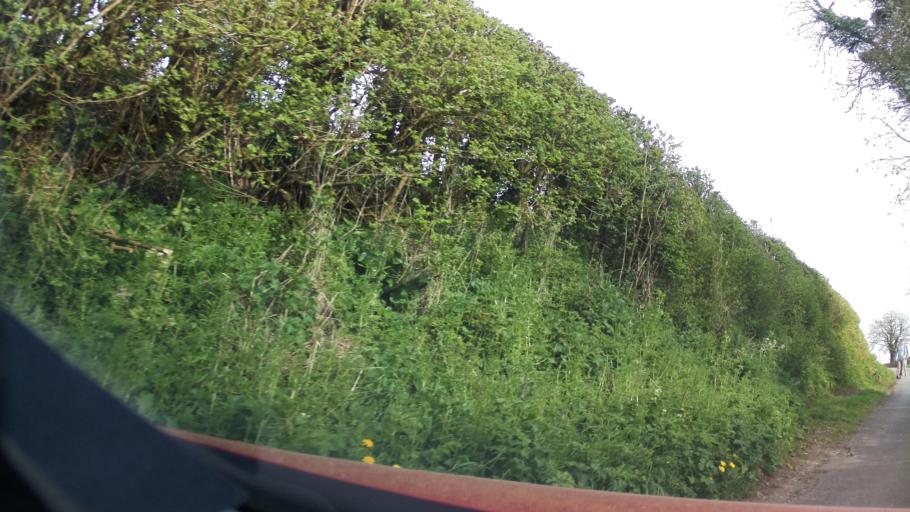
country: GB
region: England
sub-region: Somerset
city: Milborne Port
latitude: 50.9806
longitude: -2.4715
